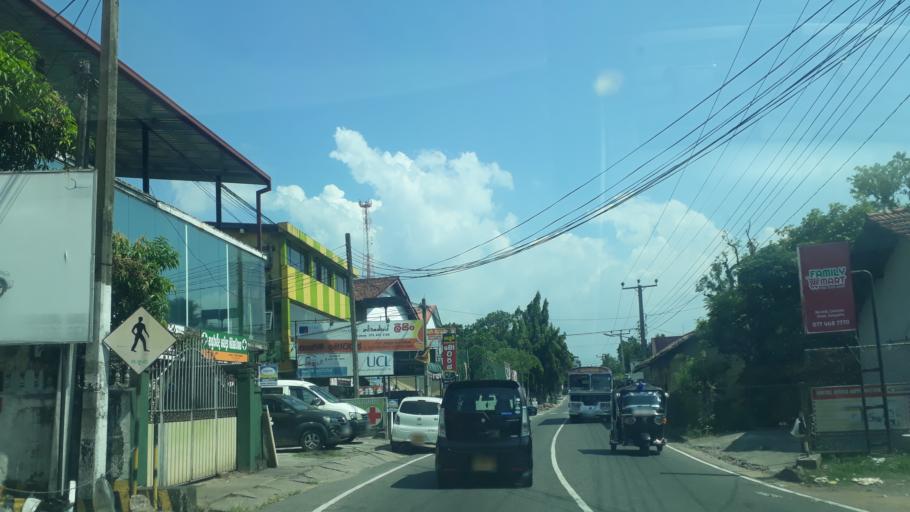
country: LK
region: Western
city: Gampaha
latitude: 7.0882
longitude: 80.0064
